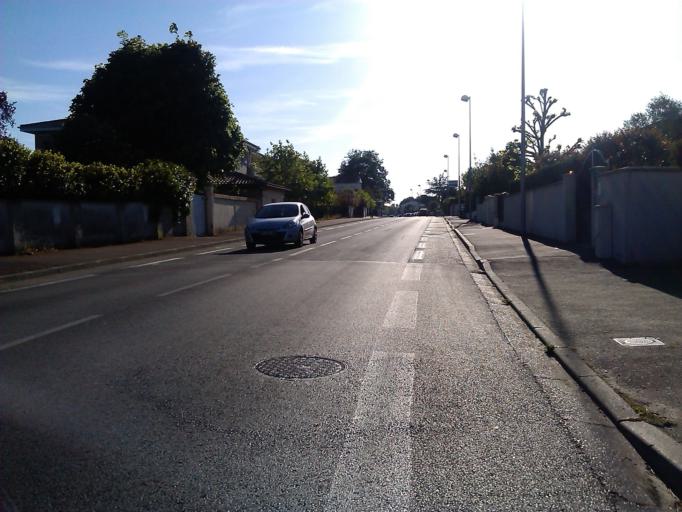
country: FR
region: Aquitaine
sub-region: Departement de la Gironde
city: Pessac
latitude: 44.8026
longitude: -0.6419
